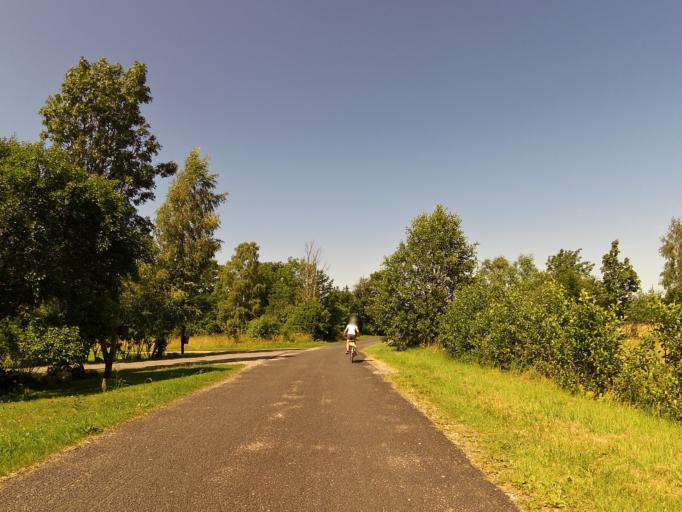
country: EE
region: Hiiumaa
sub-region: Kaerdla linn
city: Kardla
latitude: 58.7790
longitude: 22.4859
